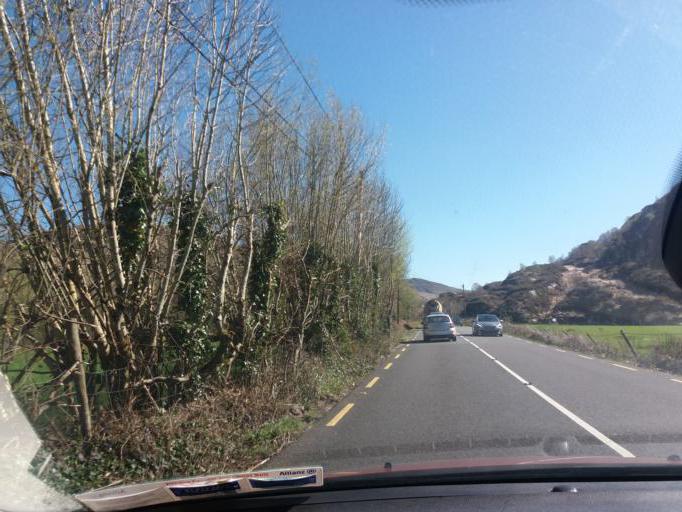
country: IE
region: Munster
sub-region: Ciarrai
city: Cill Airne
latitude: 51.9777
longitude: -9.3300
